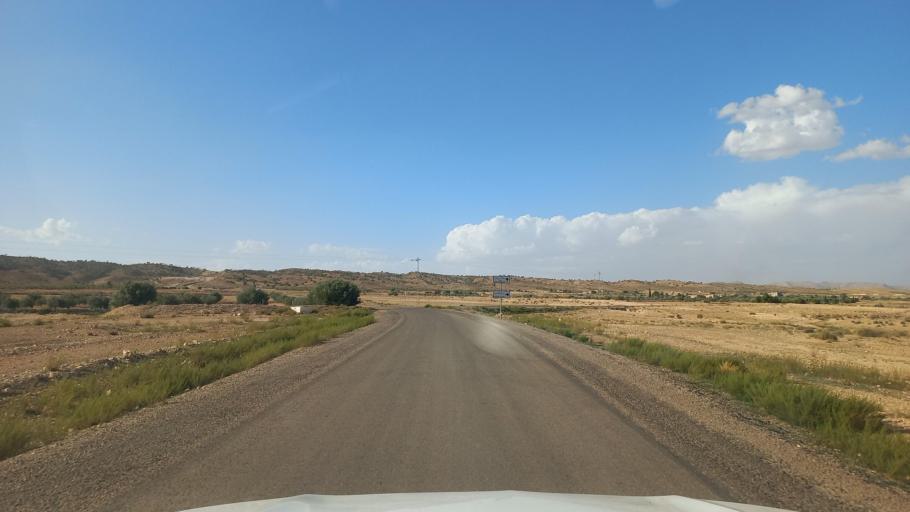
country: TN
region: Al Qasrayn
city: Sbiba
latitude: 35.3479
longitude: 8.9891
